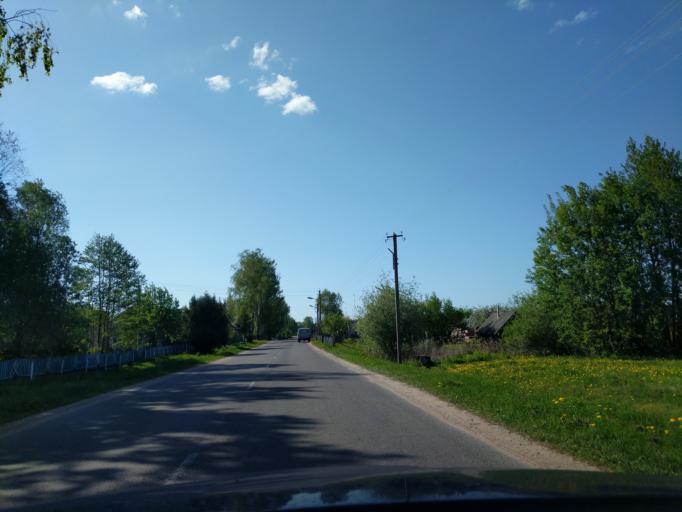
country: BY
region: Vitebsk
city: Pastavy
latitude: 55.1539
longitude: 26.9948
